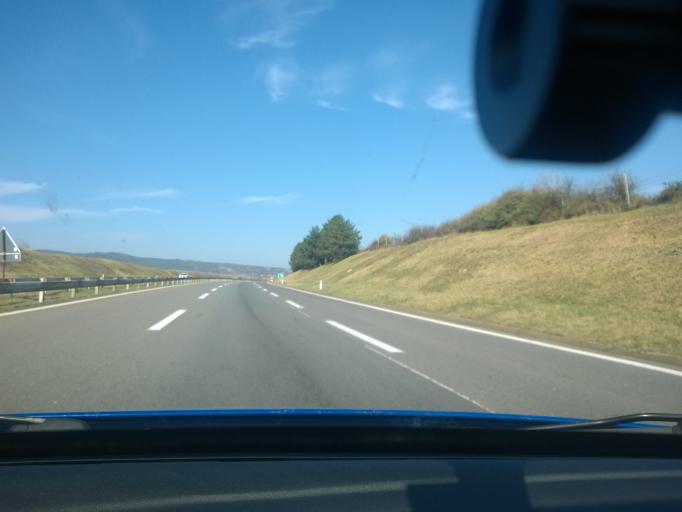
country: RS
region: Central Serbia
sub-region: Nisavski Okrug
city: Razanj
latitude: 43.6359
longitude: 21.5608
